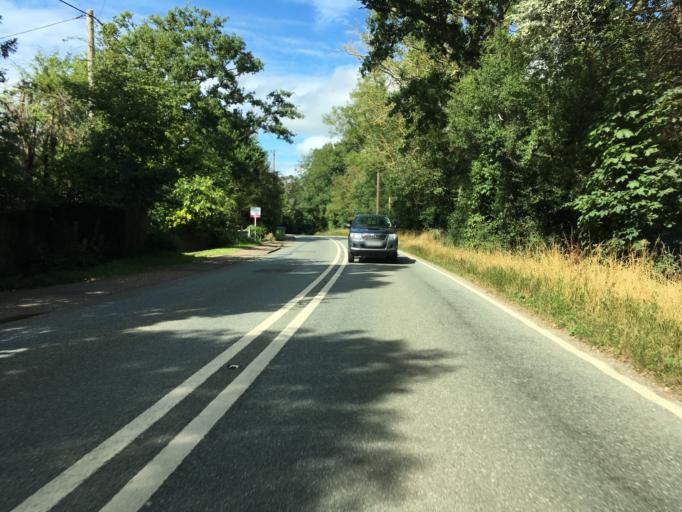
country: GB
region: England
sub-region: West Sussex
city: Southwater
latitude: 51.0605
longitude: -0.3815
